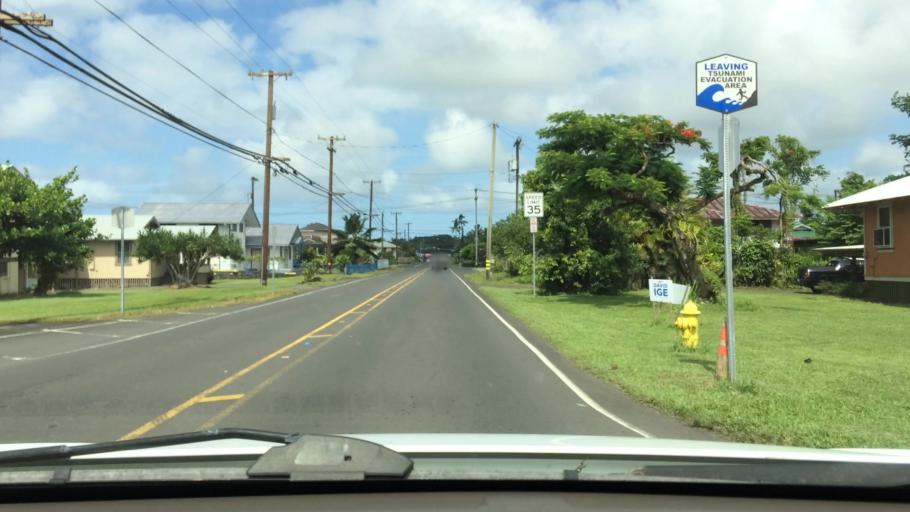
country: US
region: Hawaii
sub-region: Hawaii County
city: Hilo
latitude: 19.7117
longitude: -155.0686
